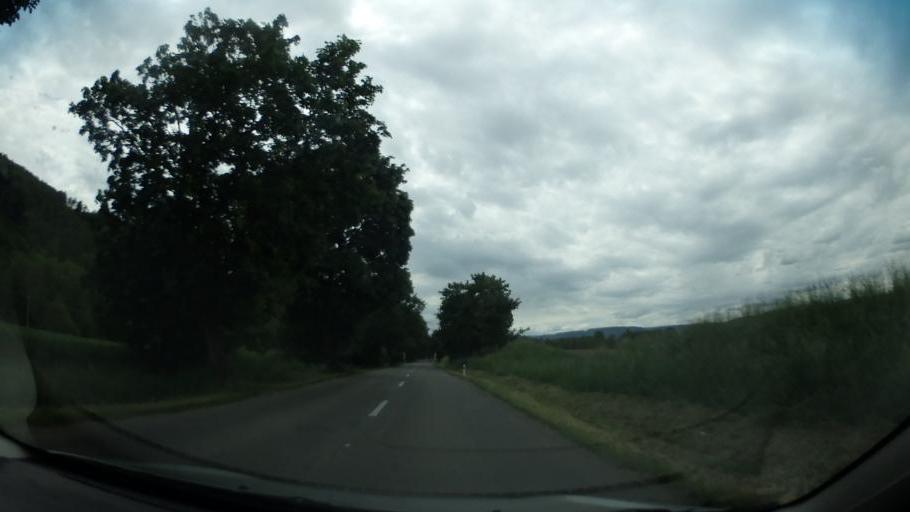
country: CZ
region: Pardubicky
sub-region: Okres Svitavy
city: Moravska Trebova
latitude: 49.7821
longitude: 16.6675
